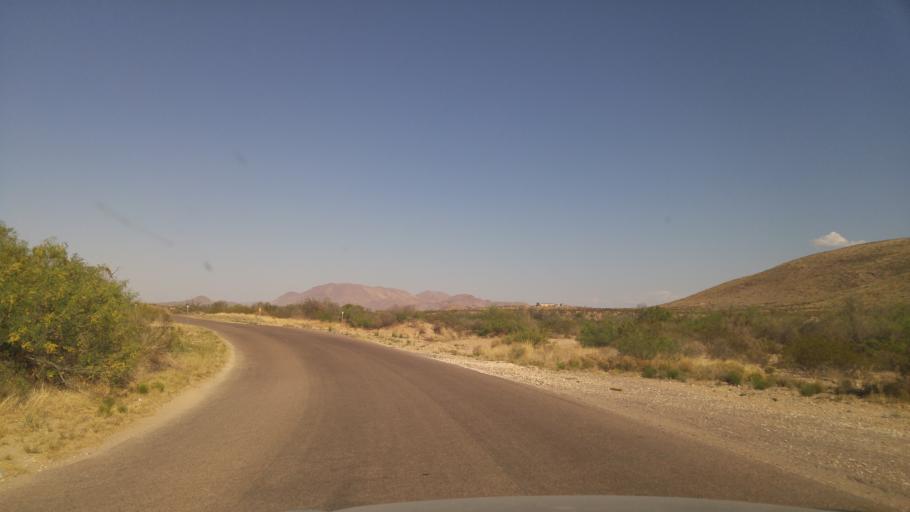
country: US
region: Texas
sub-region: Brewster County
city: Alpine
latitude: 29.5306
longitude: -103.4214
